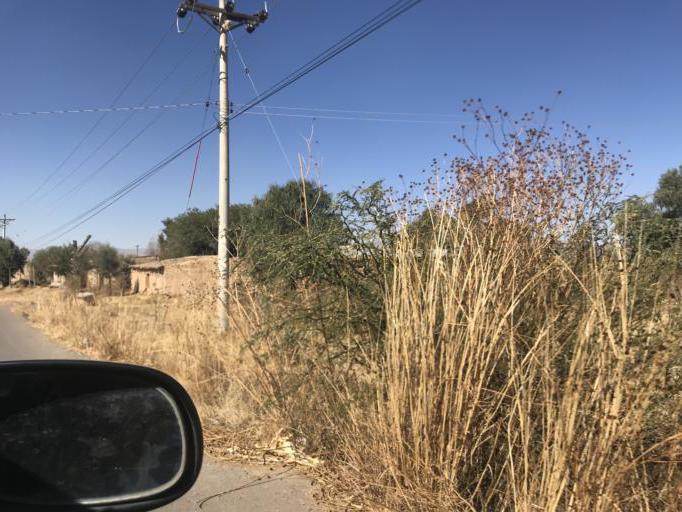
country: BO
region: Cochabamba
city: Cliza
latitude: -17.5989
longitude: -65.9610
